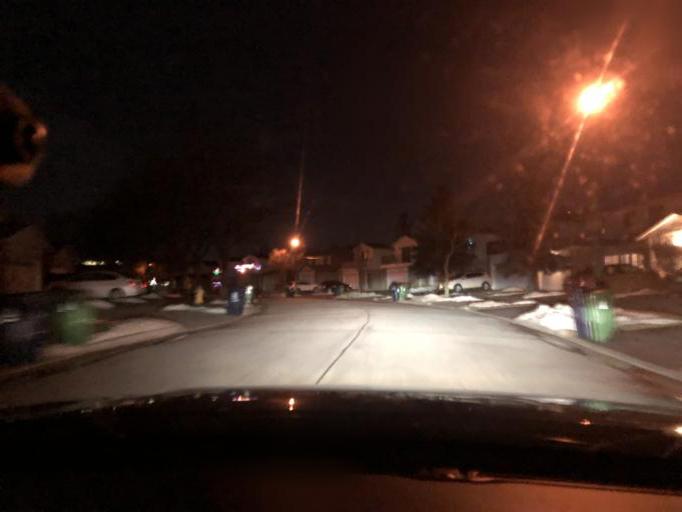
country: CA
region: Ontario
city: Scarborough
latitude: 43.7818
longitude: -79.3081
